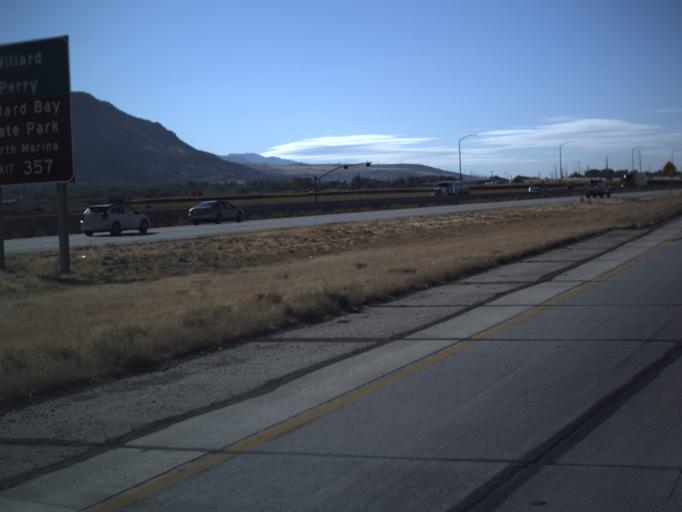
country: US
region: Utah
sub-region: Box Elder County
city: Perry
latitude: 41.4394
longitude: -112.0574
